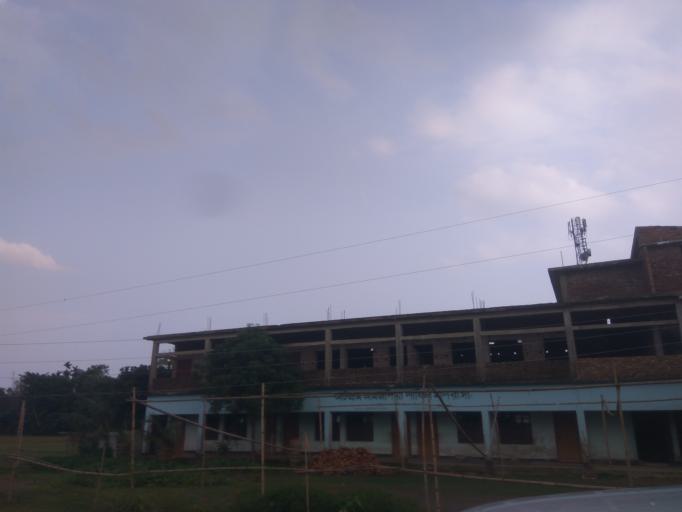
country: IN
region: Assam
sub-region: Karimganj
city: Karimganj
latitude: 24.9871
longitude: 92.4001
